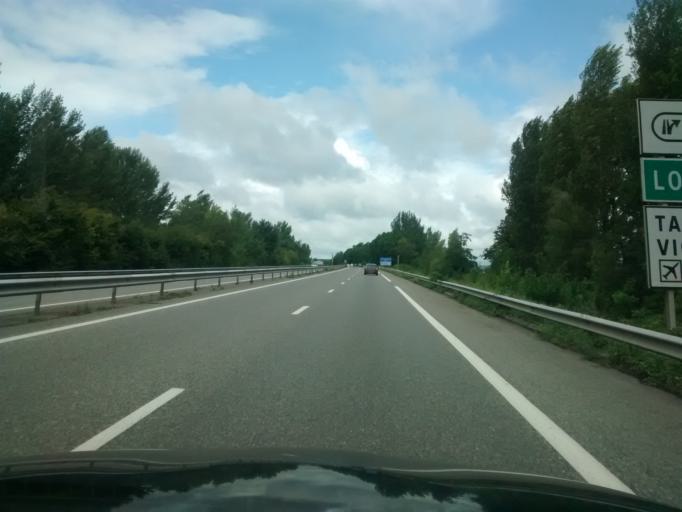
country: FR
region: Midi-Pyrenees
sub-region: Departement des Hautes-Pyrenees
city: Juillan
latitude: 43.2130
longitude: 0.0340
